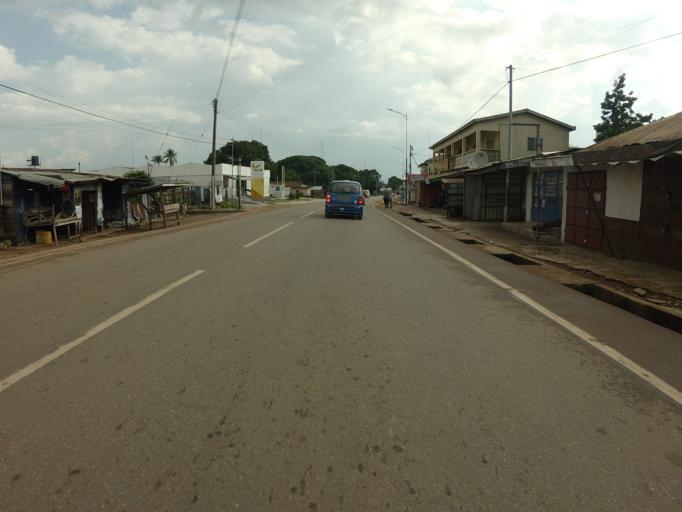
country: GH
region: Volta
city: Hohoe
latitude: 7.1519
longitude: 0.4747
